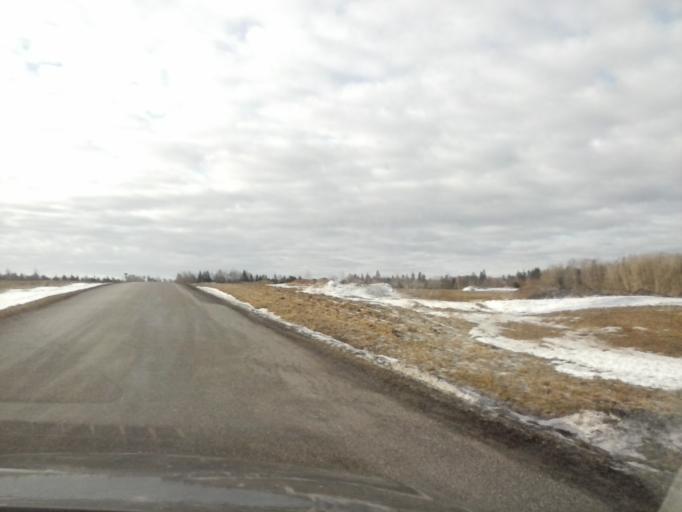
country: EE
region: Tartu
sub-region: Elva linn
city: Elva
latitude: 58.0382
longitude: 26.3545
